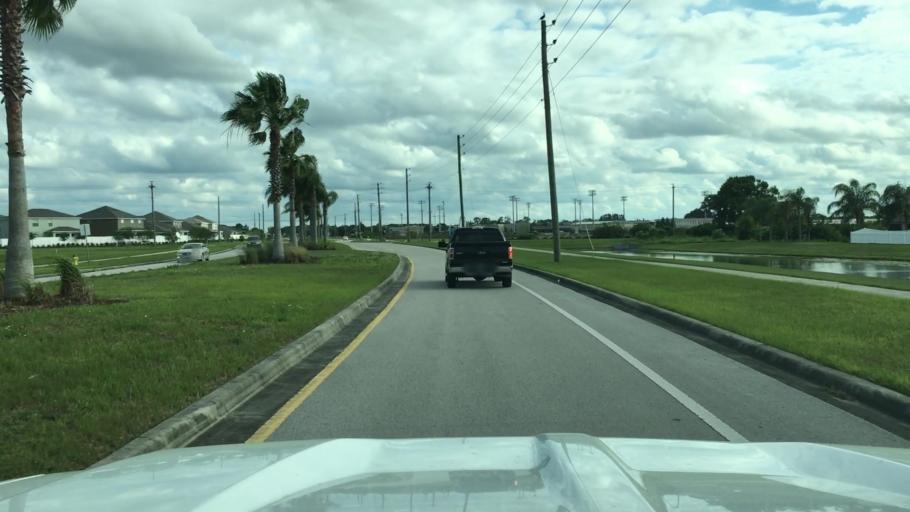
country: US
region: Florida
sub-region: Hillsborough County
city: Ruskin
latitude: 27.7292
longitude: -82.4020
